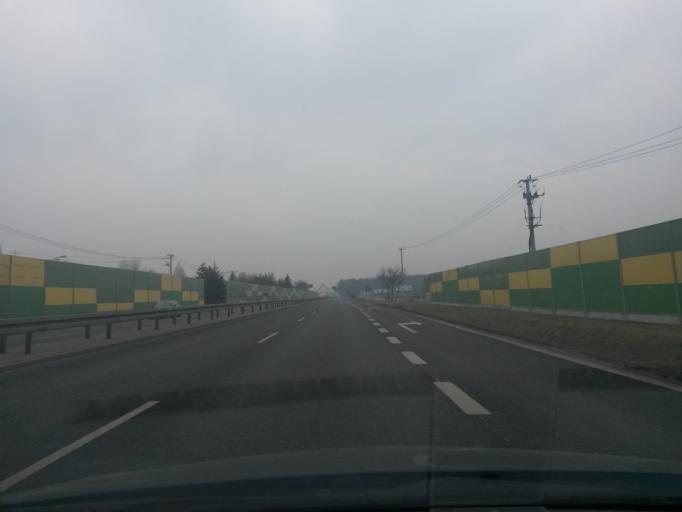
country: PL
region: Masovian Voivodeship
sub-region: Powiat legionowski
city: Serock
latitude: 52.4834
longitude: 21.0410
